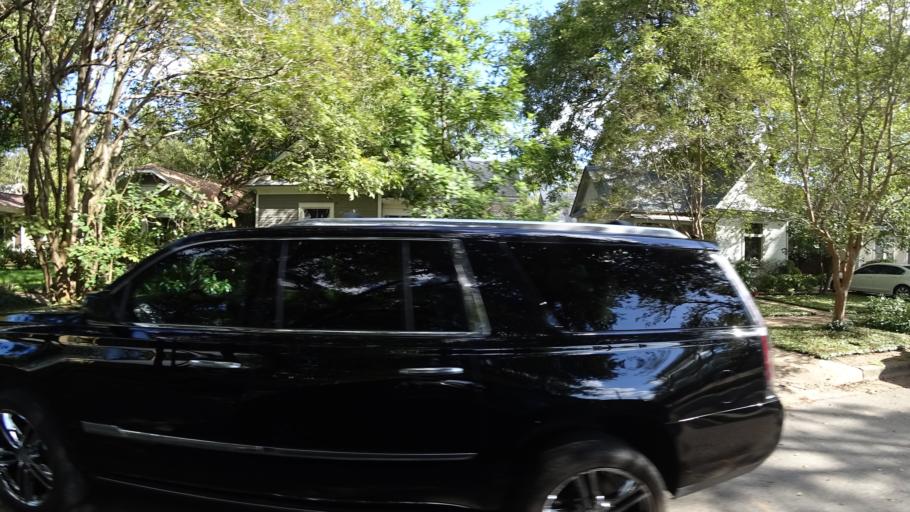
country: US
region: Texas
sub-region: Travis County
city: Austin
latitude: 30.3078
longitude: -97.7313
